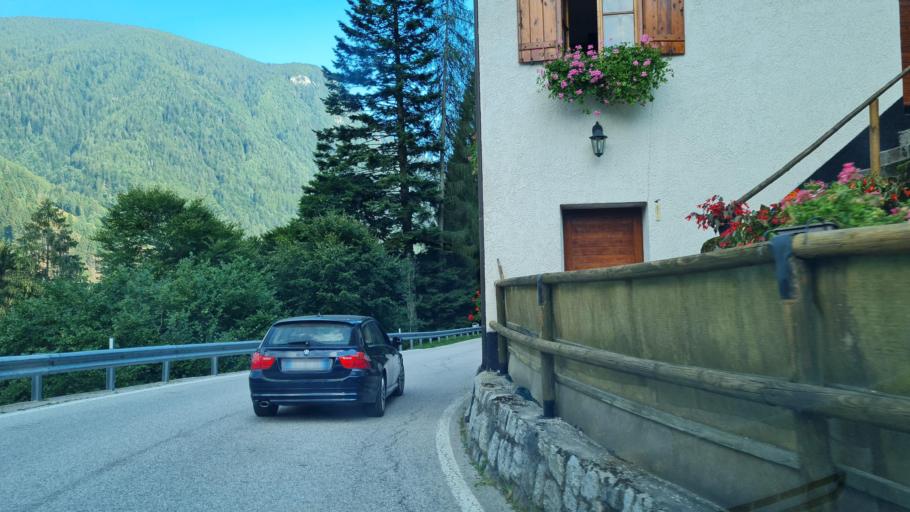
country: IT
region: Trentino-Alto Adige
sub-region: Provincia di Trento
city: Carzano
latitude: 46.1155
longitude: 11.4923
